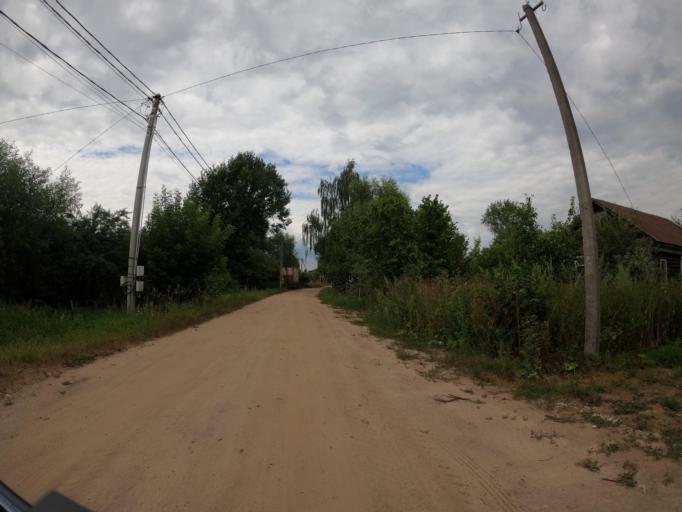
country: RU
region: Moskovskaya
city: Bronnitsy
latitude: 55.4816
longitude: 38.2551
